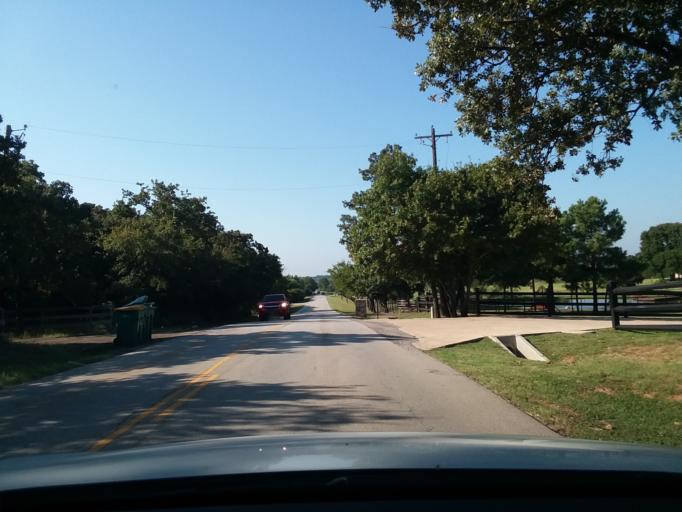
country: US
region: Texas
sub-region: Denton County
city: Bartonville
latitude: 33.0640
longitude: -97.1316
